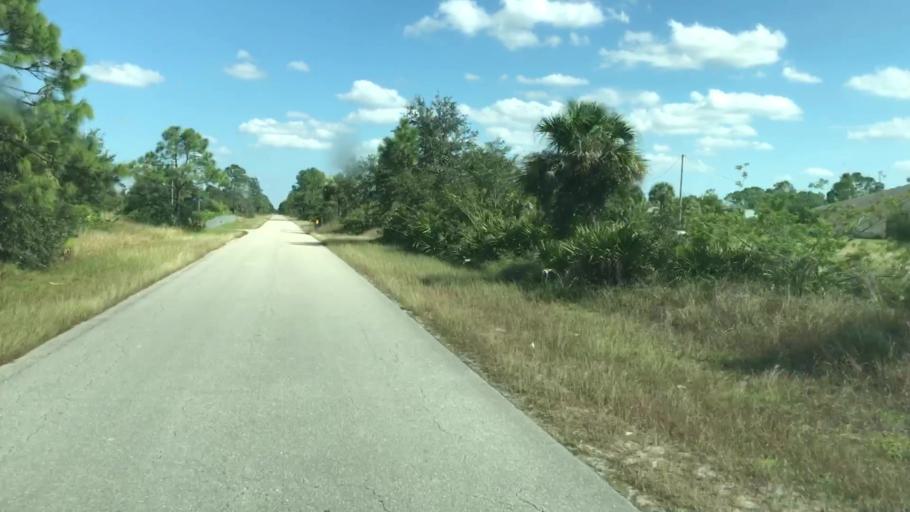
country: US
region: Florida
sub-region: Lee County
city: Lehigh Acres
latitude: 26.6284
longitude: -81.6330
